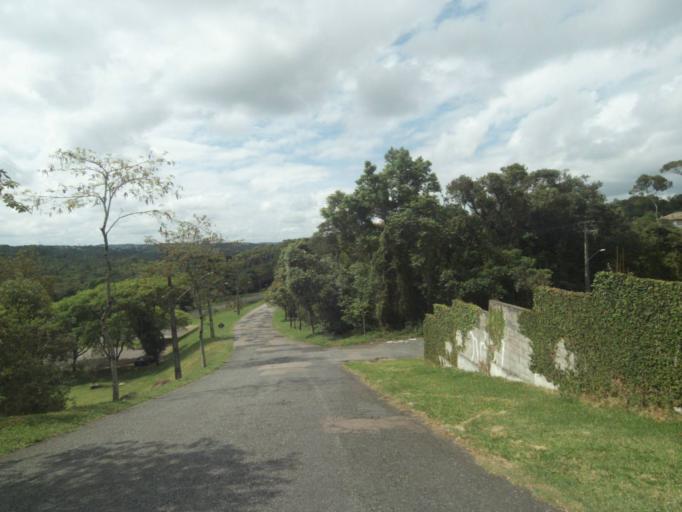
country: BR
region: Parana
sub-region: Curitiba
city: Curitiba
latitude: -25.3818
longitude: -49.2841
